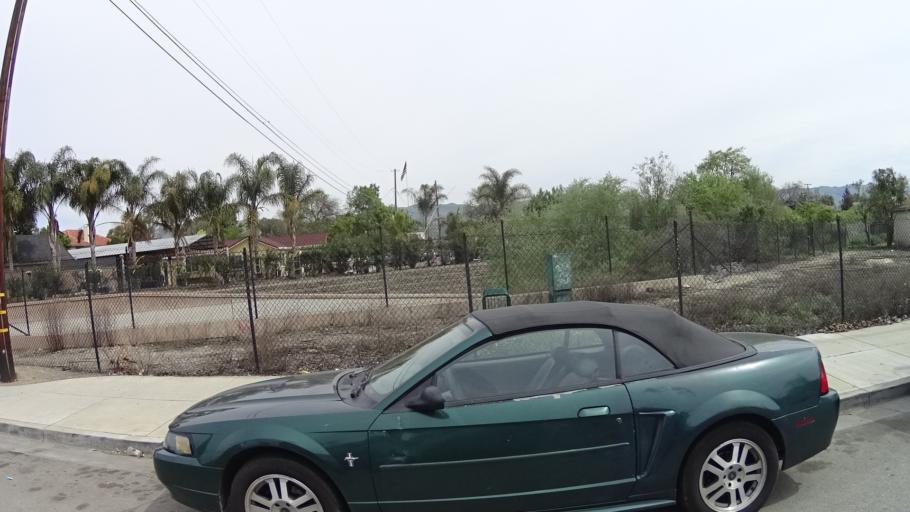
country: US
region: California
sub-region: Santa Clara County
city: Alum Rock
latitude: 37.3543
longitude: -121.8481
